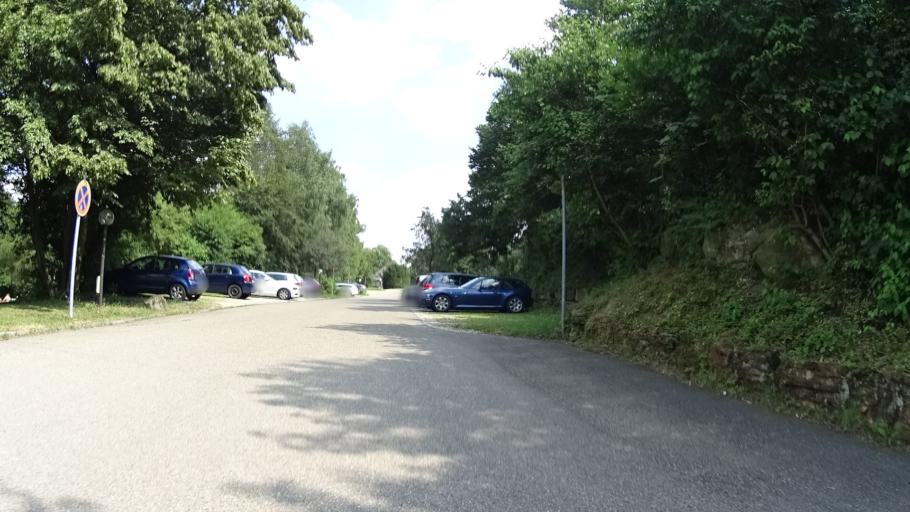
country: DE
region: Baden-Wuerttemberg
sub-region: Regierungsbezirk Stuttgart
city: Goeppingen
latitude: 48.7000
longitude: 9.6418
